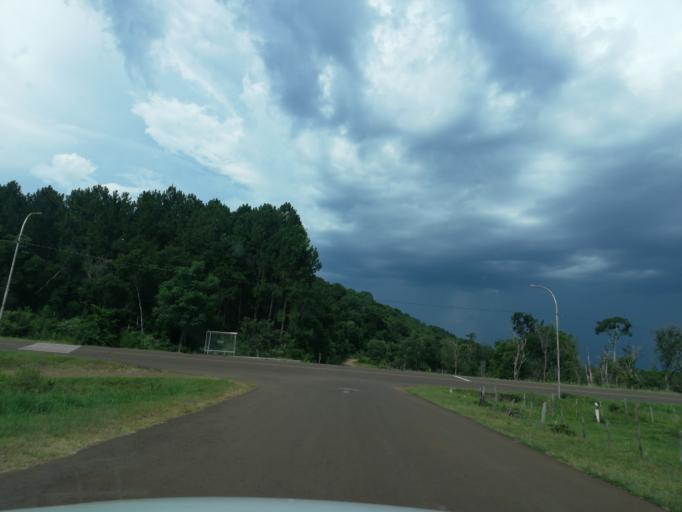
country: AR
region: Misiones
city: Cerro Azul
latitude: -27.5706
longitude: -55.4974
